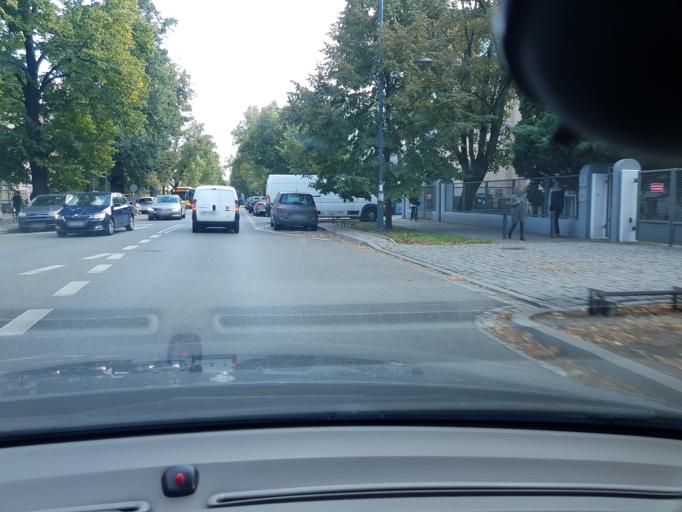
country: PL
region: Masovian Voivodeship
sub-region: Warszawa
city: Praga Polnoc
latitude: 52.2360
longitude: 21.0532
